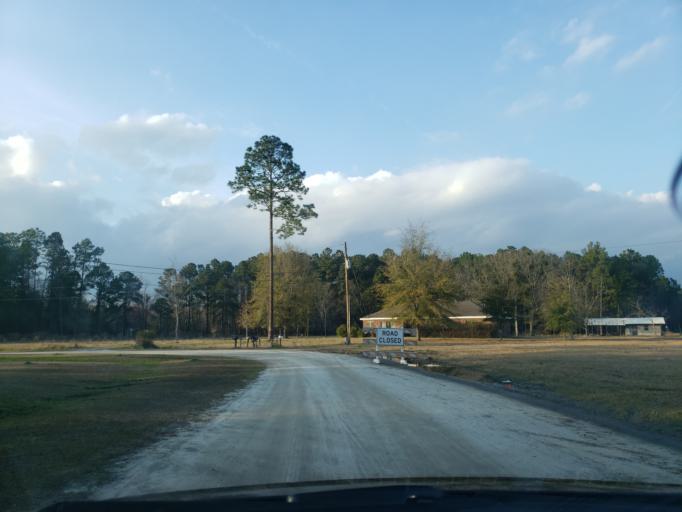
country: US
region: Georgia
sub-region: Chatham County
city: Bloomingdale
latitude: 32.1495
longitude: -81.2882
